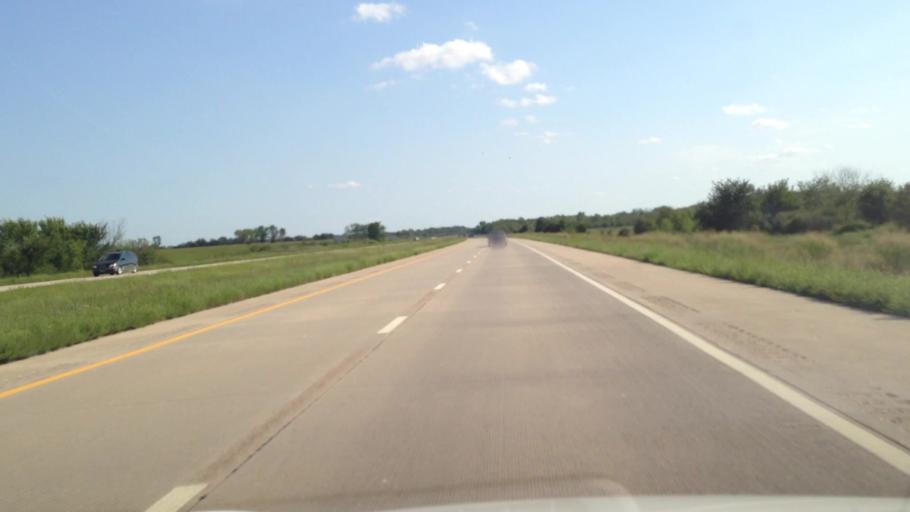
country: US
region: Kansas
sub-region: Bourbon County
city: Fort Scott
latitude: 37.9207
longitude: -94.7046
